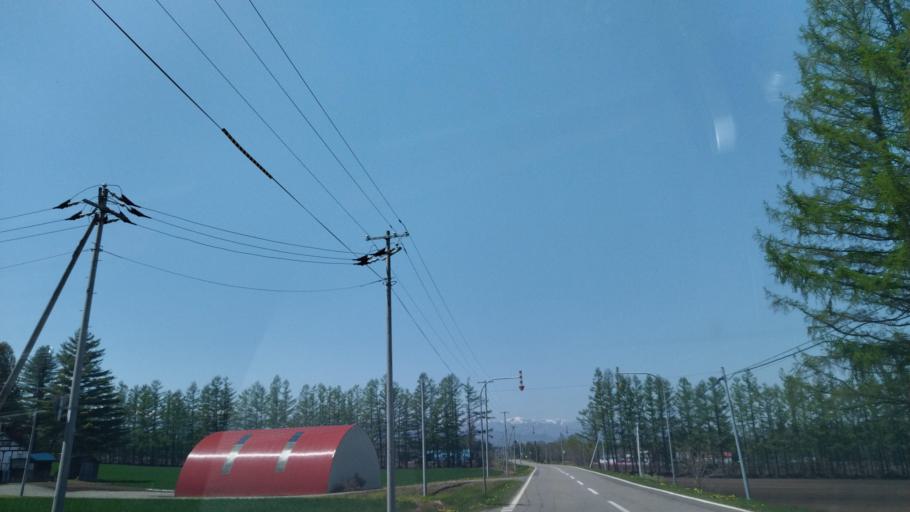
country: JP
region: Hokkaido
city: Obihiro
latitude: 42.9082
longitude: 142.9912
